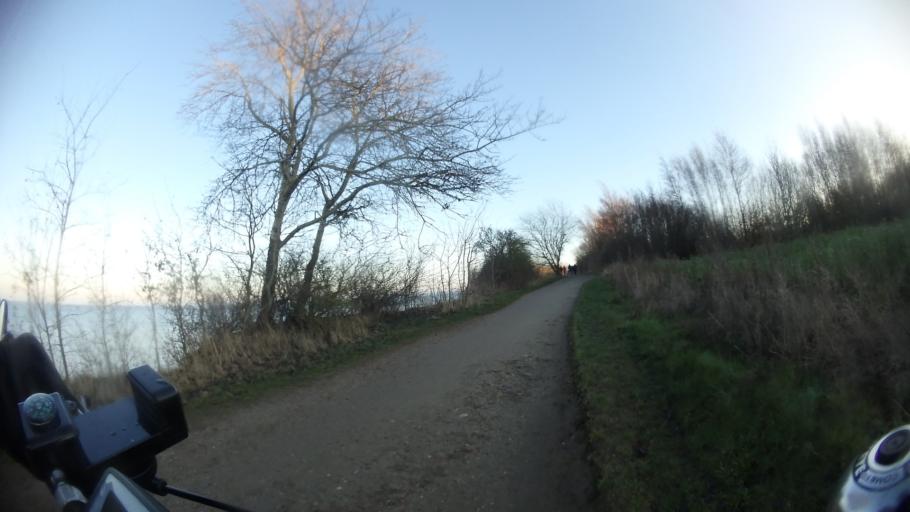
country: DE
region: Schleswig-Holstein
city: Travemuende
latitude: 53.9927
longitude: 10.8631
